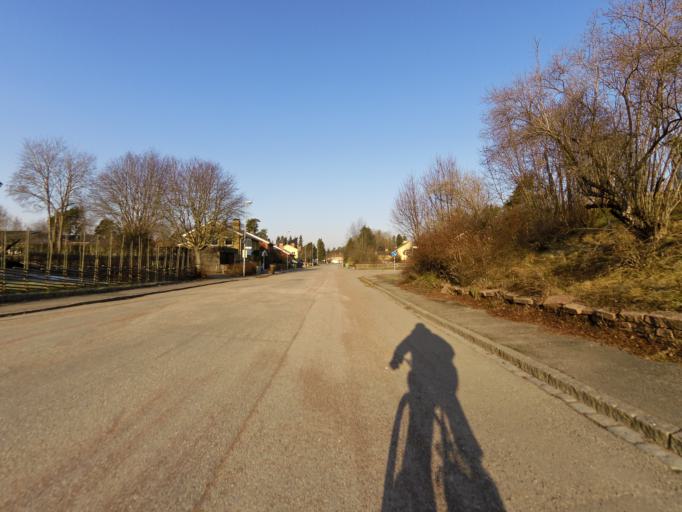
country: SE
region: Gaevleborg
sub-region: Gavle Kommun
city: Gavle
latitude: 60.6586
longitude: 17.1390
